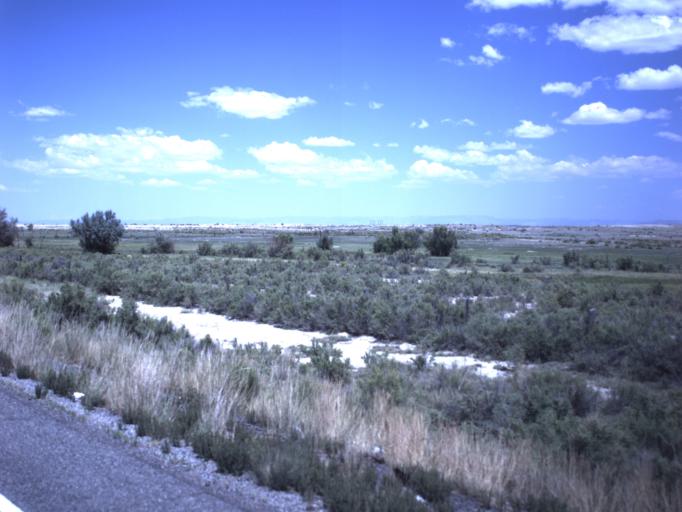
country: US
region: Utah
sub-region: Emery County
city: Castle Dale
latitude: 39.2338
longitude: -110.9927
